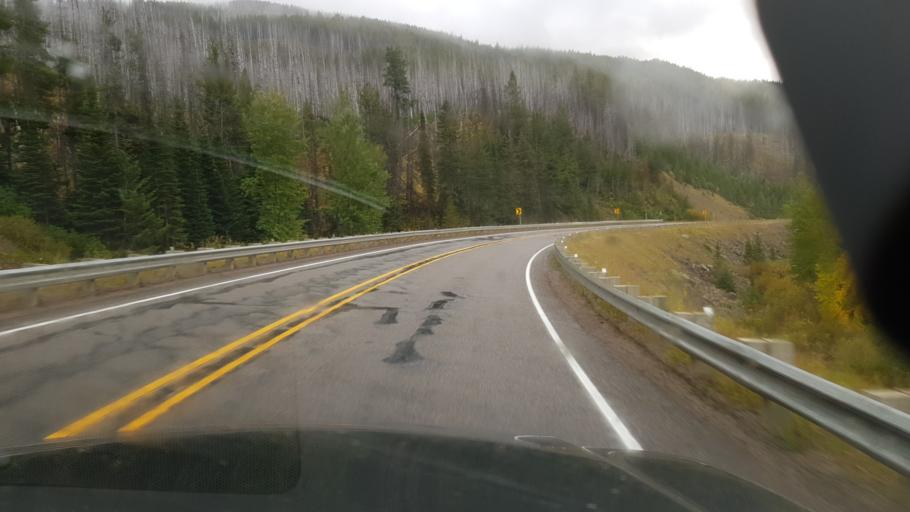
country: US
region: Montana
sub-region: Glacier County
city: South Browning
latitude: 48.3038
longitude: -113.3642
